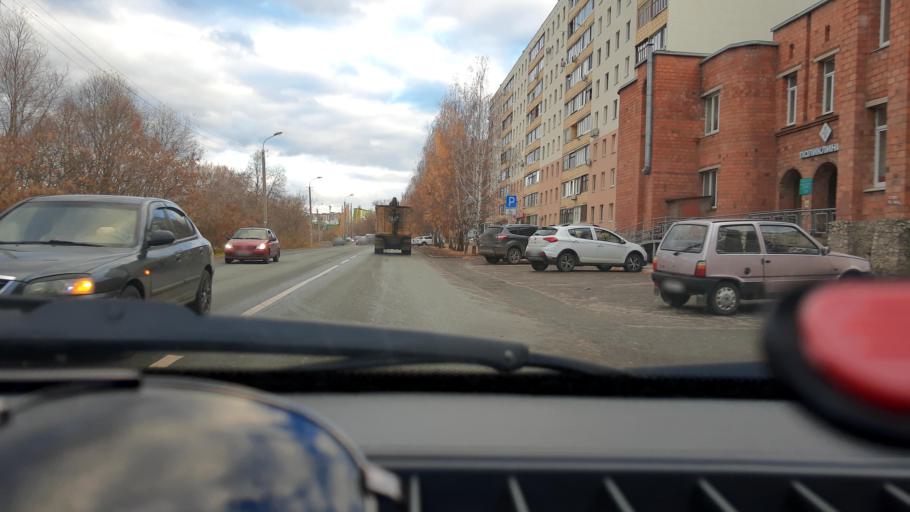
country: RU
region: Bashkortostan
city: Mikhaylovka
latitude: 54.7075
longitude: 55.8404
